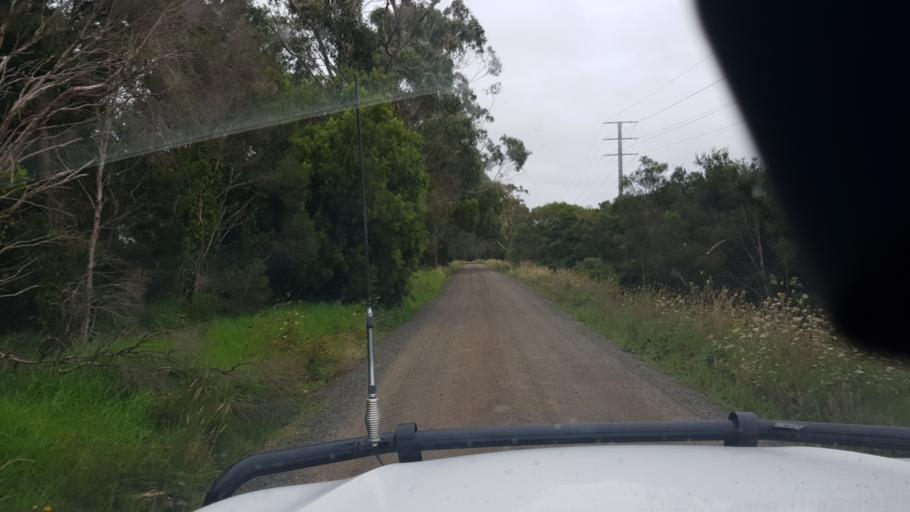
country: AU
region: Victoria
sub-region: Cardinia
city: Bunyip
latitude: -38.1036
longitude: 145.7521
